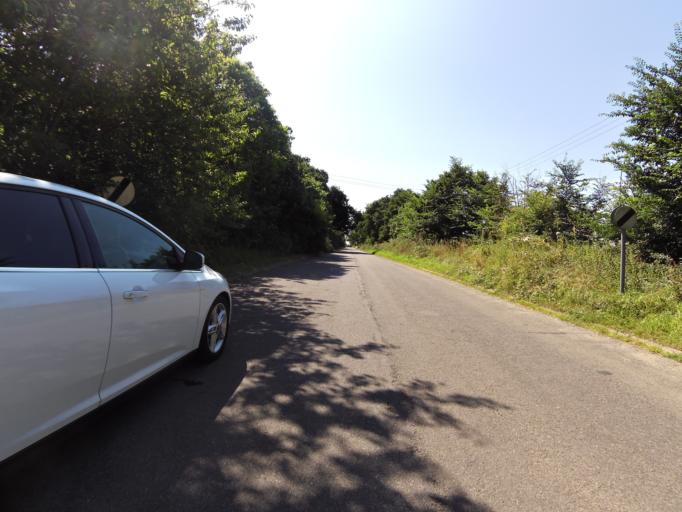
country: GB
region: England
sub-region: Suffolk
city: Capel Saint Mary
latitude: 52.0145
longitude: 1.0677
